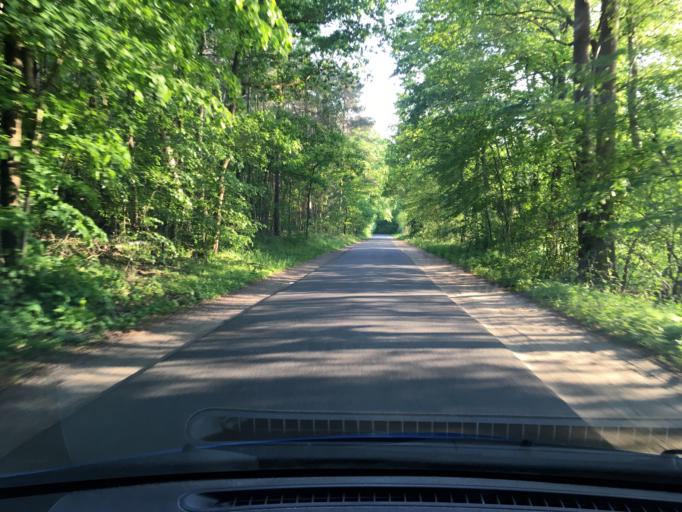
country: DE
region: Lower Saxony
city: Rullstorf
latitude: 53.2835
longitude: 10.5680
